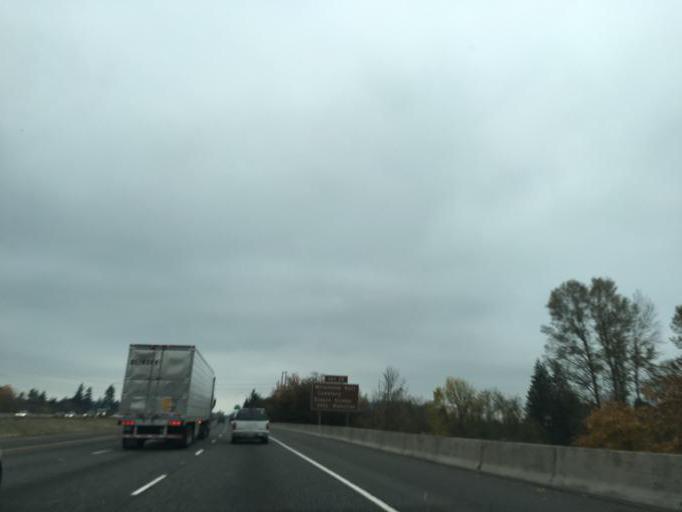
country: US
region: Oregon
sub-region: Multnomah County
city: Lents
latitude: 45.4704
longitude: -122.5651
